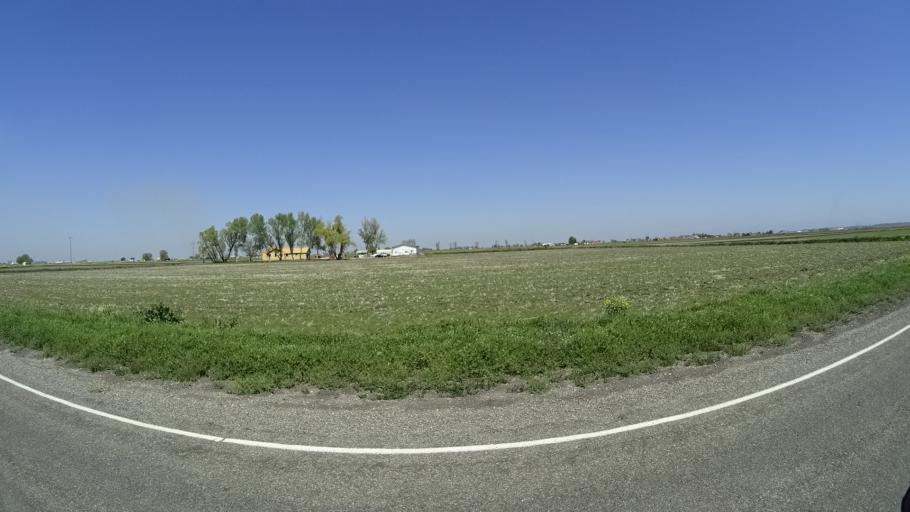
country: US
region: California
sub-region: Glenn County
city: Willows
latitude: 39.5580
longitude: -122.0592
